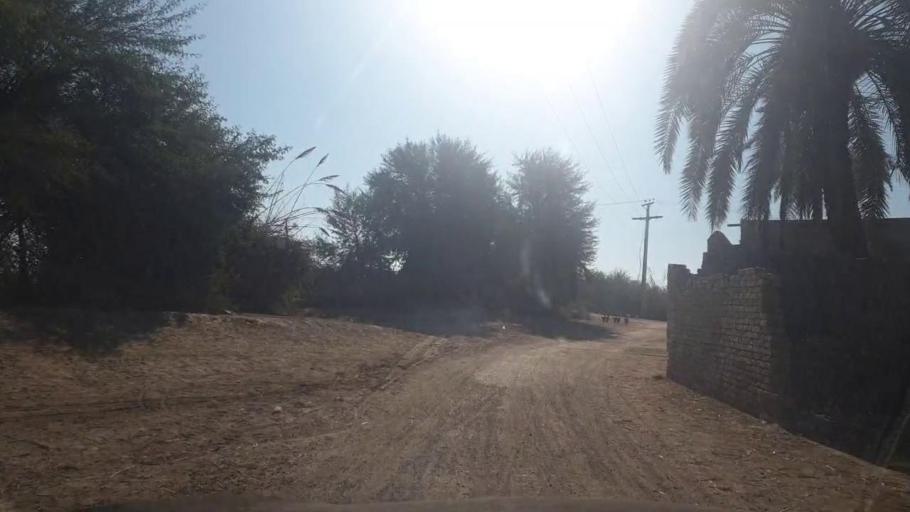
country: PK
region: Sindh
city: Ghotki
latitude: 27.9829
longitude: 69.3260
